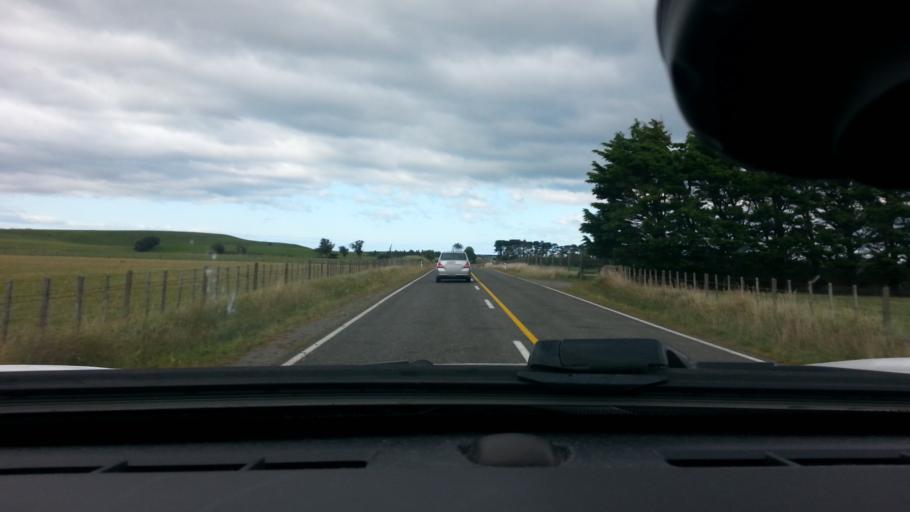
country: NZ
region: Wellington
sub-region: Upper Hutt City
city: Upper Hutt
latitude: -41.3792
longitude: 175.1795
